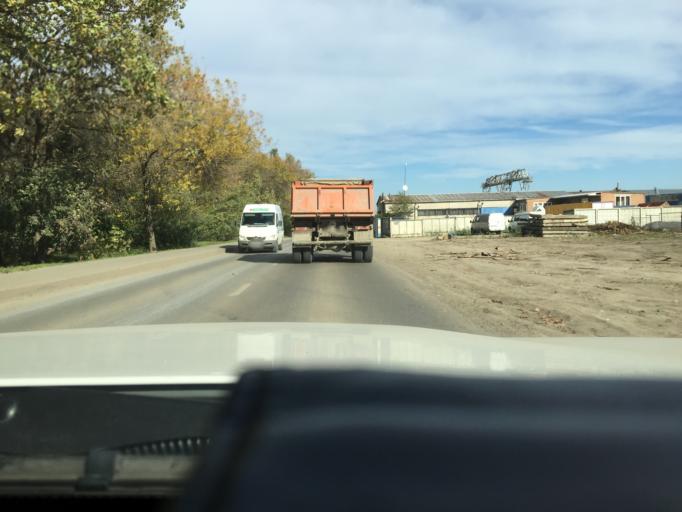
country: RU
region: Rostov
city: Imeni Chkalova
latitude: 47.2919
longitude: 39.8037
